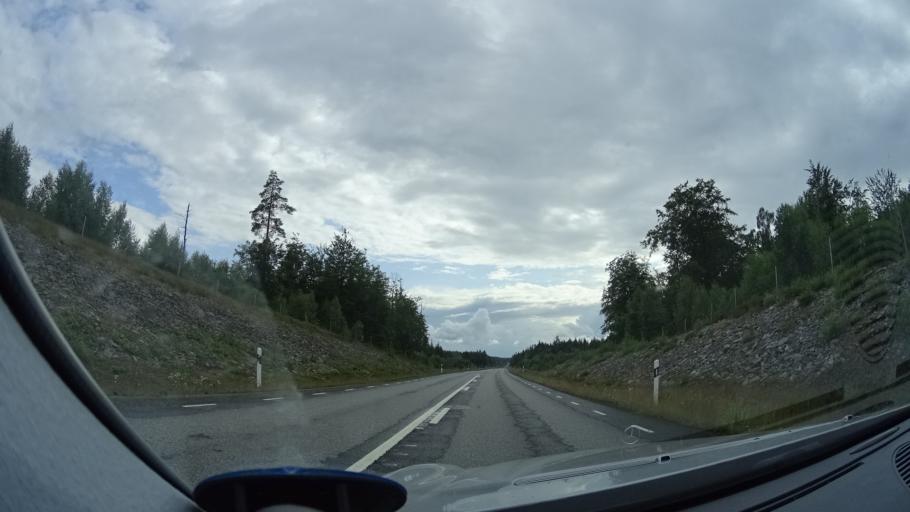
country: SE
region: Blekinge
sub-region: Karlshamns Kommun
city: Svangsta
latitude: 56.2738
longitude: 14.8597
